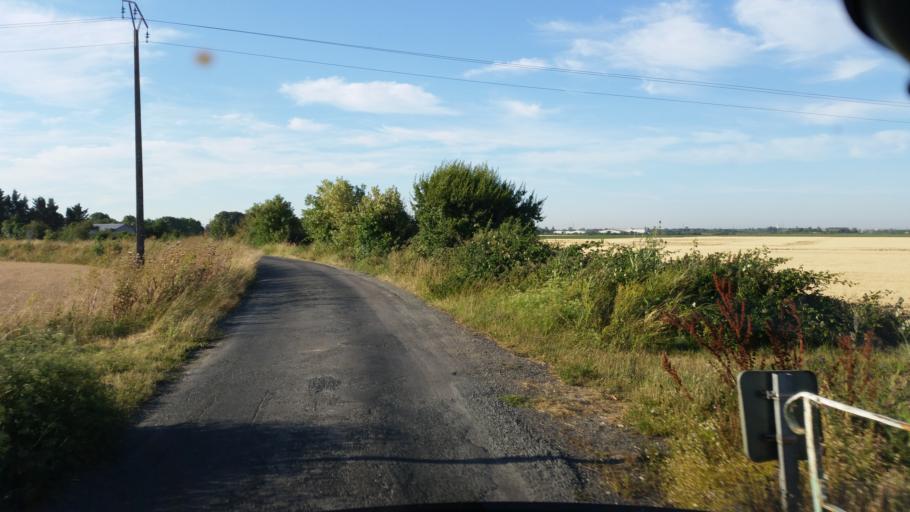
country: FR
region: Poitou-Charentes
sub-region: Departement de la Charente-Maritime
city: Marans
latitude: 46.3006
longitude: -0.9944
